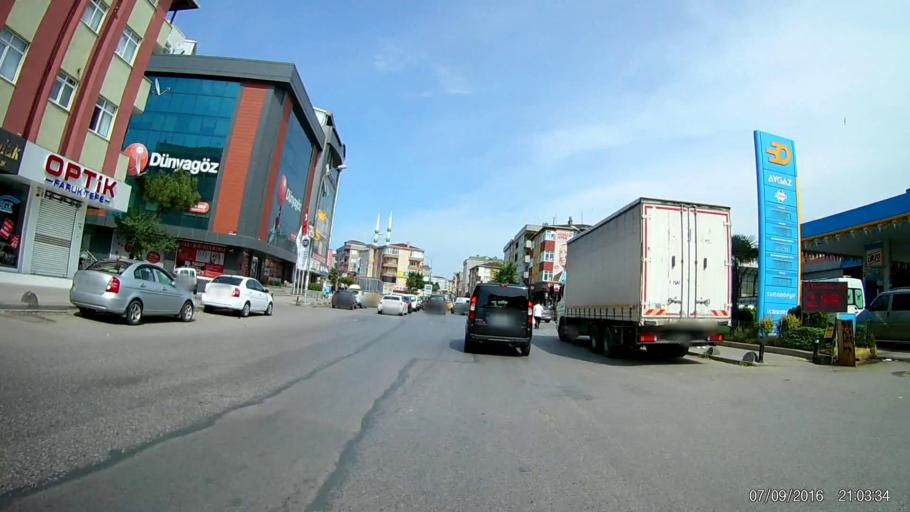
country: TR
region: Istanbul
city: Sultanbeyli
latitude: 40.9684
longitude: 29.2532
